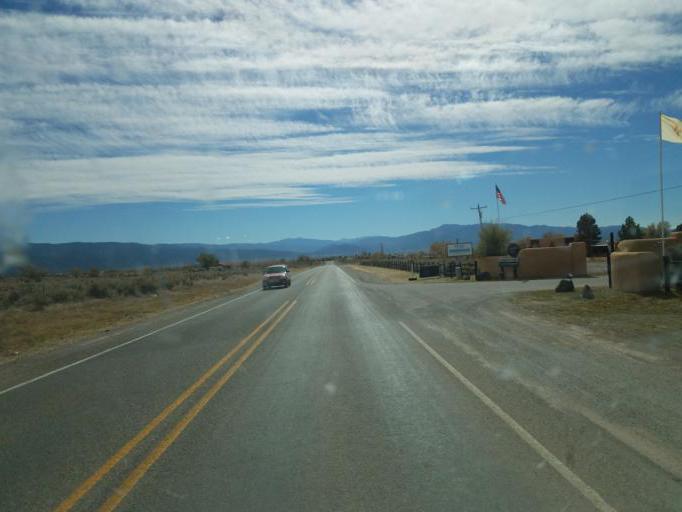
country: US
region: New Mexico
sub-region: Taos County
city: Arroyo Seco
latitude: 36.4700
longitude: -105.5937
